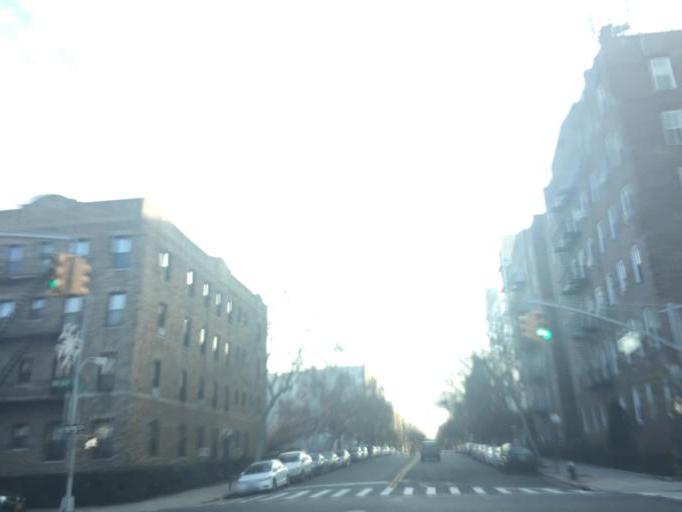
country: US
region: New York
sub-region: Queens County
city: Long Island City
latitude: 40.7471
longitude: -73.9208
